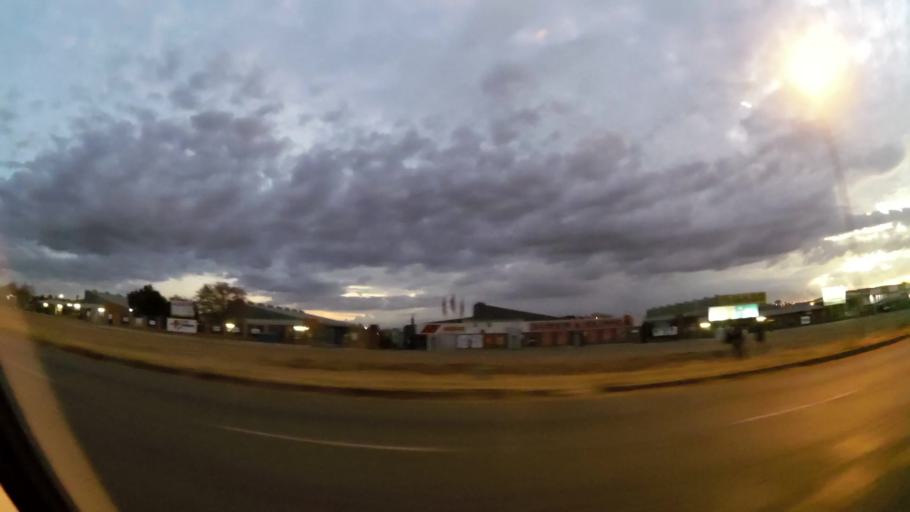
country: ZA
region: Limpopo
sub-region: Capricorn District Municipality
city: Polokwane
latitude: -23.8732
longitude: 29.4391
